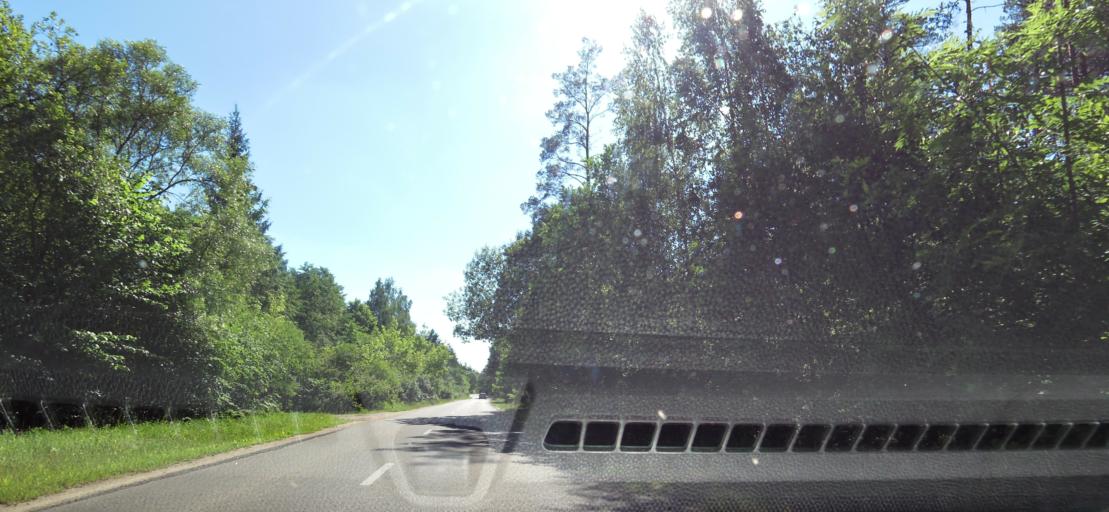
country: LT
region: Vilnius County
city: Rasos
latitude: 54.7558
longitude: 25.3378
